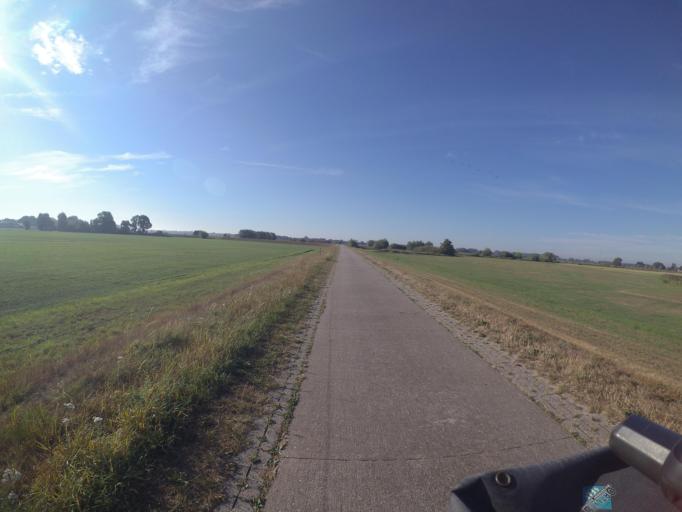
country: NL
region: Overijssel
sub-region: Gemeente Zwartewaterland
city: Hasselt
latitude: 52.5632
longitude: 6.1099
